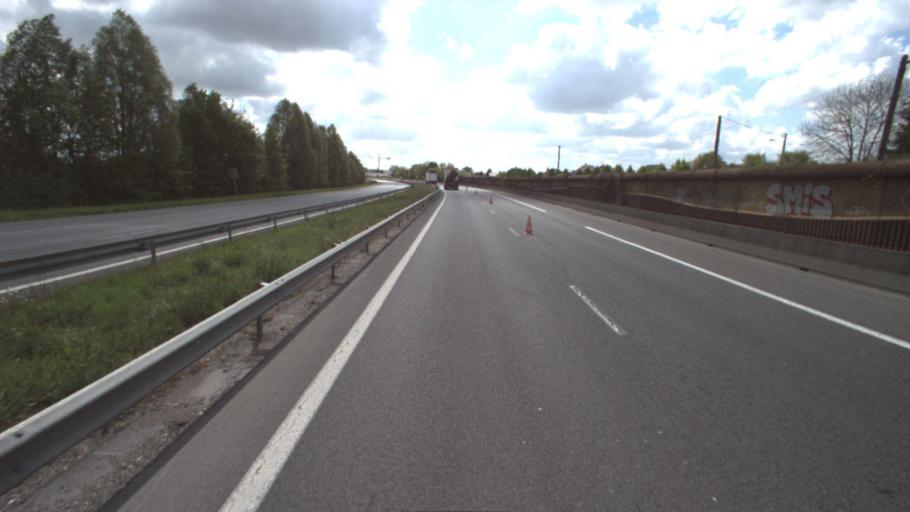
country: FR
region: Ile-de-France
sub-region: Departement de Seine-et-Marne
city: Fontenay-Tresigny
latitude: 48.7061
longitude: 2.8814
